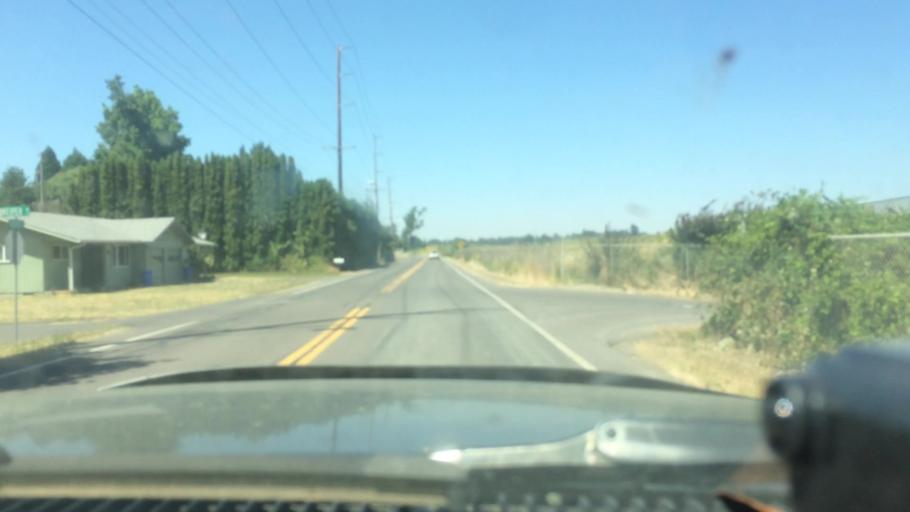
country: US
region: Oregon
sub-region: Lane County
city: Eugene
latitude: 44.0990
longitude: -123.1142
